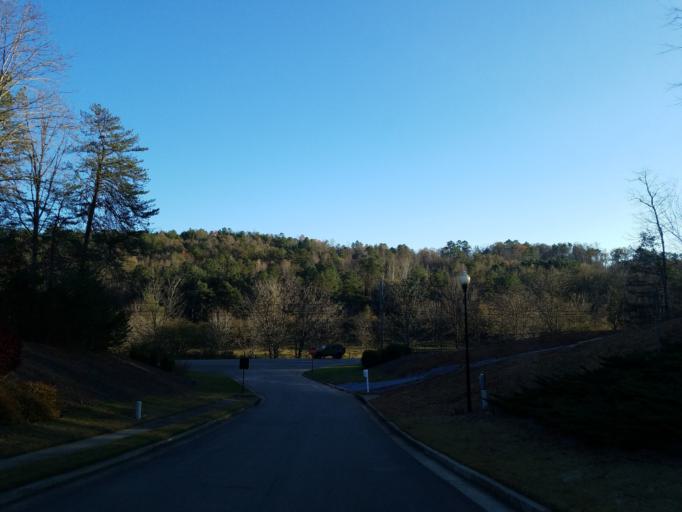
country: US
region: Georgia
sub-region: Cherokee County
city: Ball Ground
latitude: 34.3427
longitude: -84.3705
